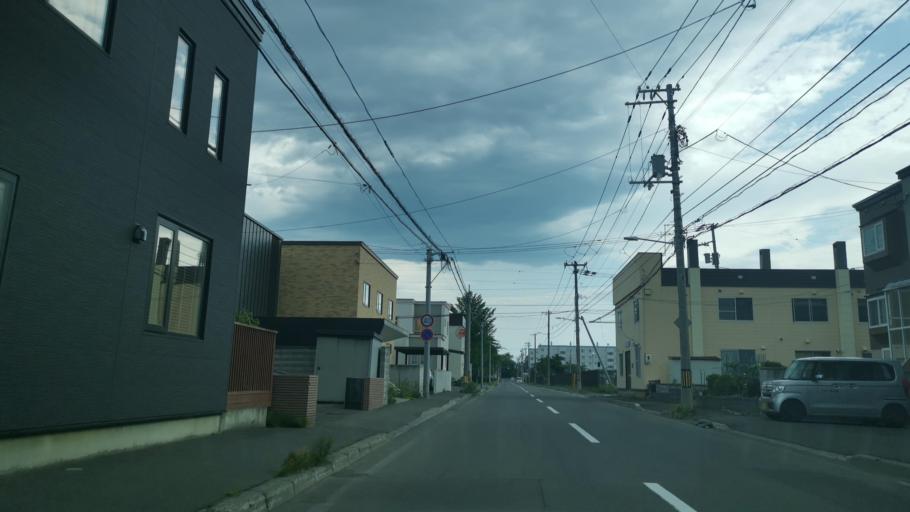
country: JP
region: Hokkaido
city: Sapporo
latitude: 43.0250
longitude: 141.3491
